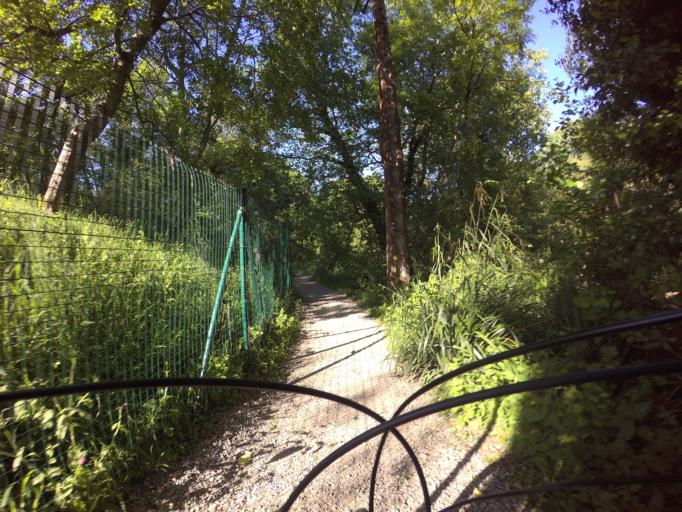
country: FR
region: Brittany
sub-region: Departement du Finistere
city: Quimper
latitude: 48.0121
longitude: -4.1163
